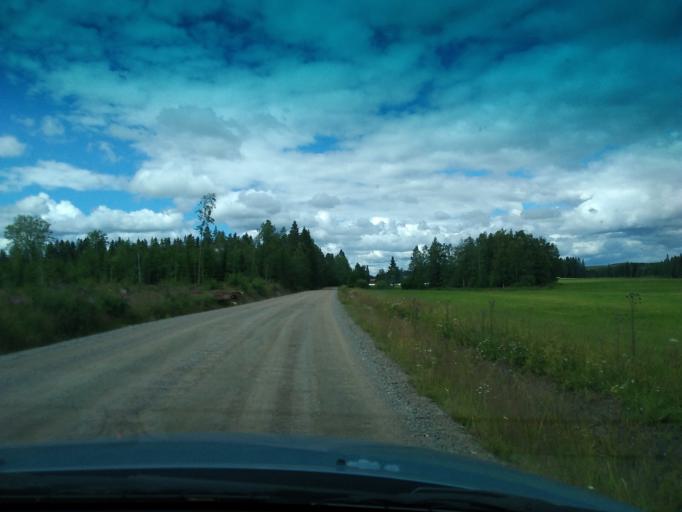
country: FI
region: Central Finland
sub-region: Saarijaervi-Viitasaari
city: Karstula
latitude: 62.7896
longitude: 24.9749
